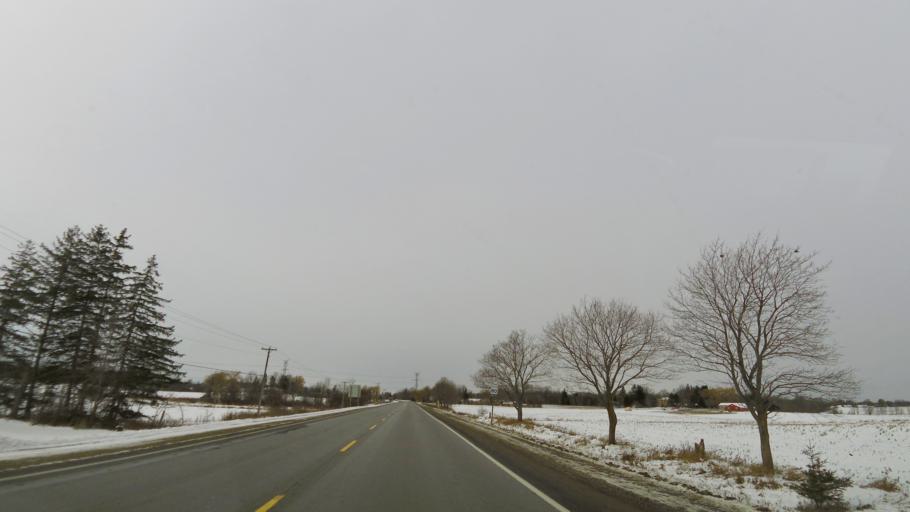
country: CA
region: Ontario
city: Ancaster
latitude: 43.2842
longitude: -80.0764
